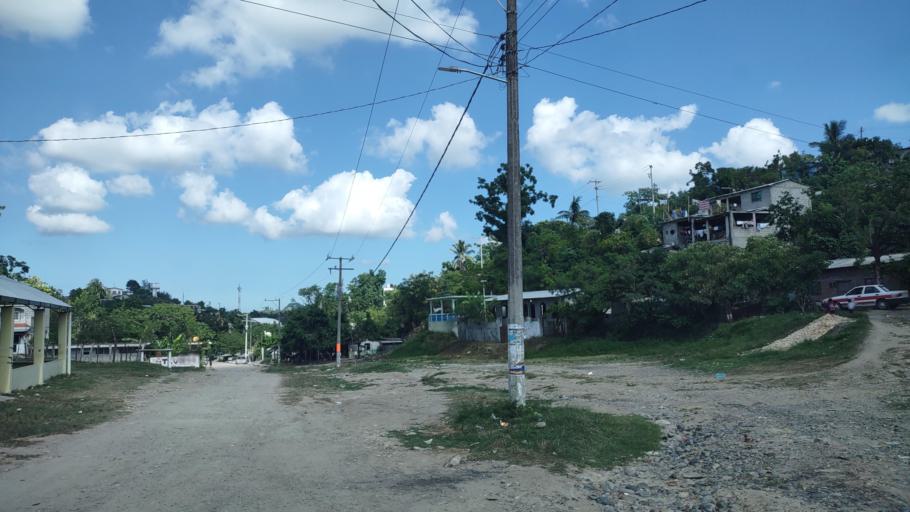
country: MM
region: Shan
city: Taunggyi
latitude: 20.5821
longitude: 97.3771
